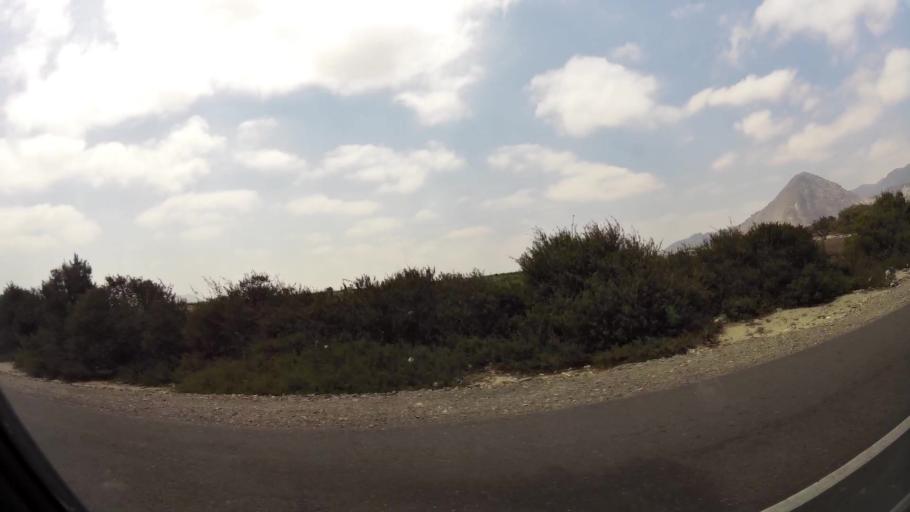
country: PE
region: La Libertad
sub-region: Ascope
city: Paijan
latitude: -7.6680
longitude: -79.3288
